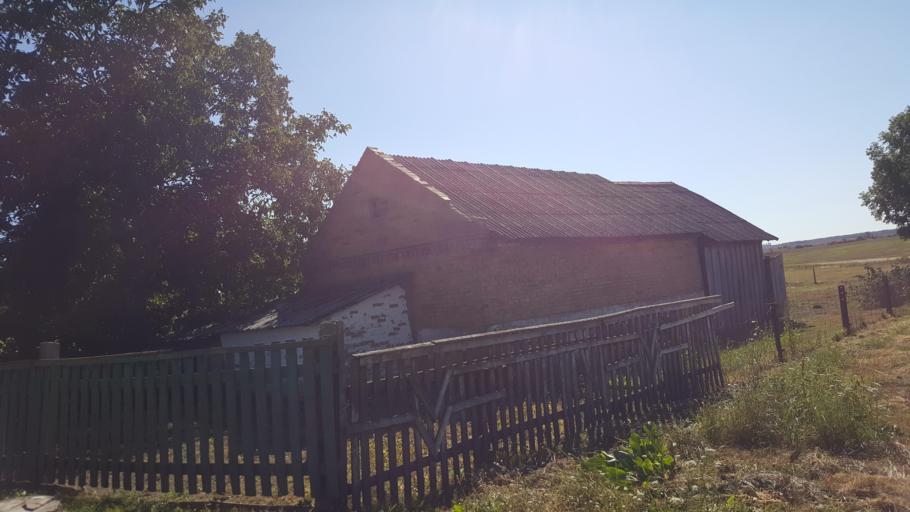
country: BY
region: Brest
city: Vysokaye
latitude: 52.2614
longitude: 23.5263
